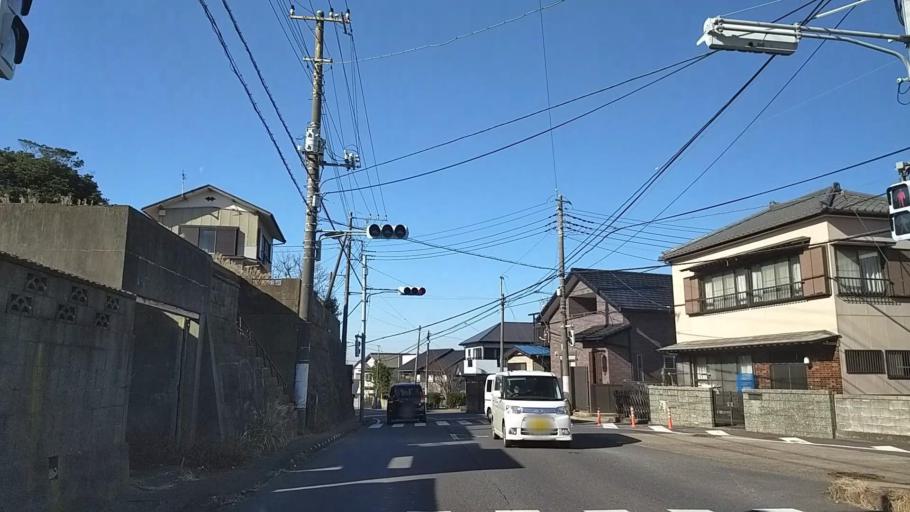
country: JP
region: Chiba
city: Hasaki
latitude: 35.7327
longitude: 140.8509
